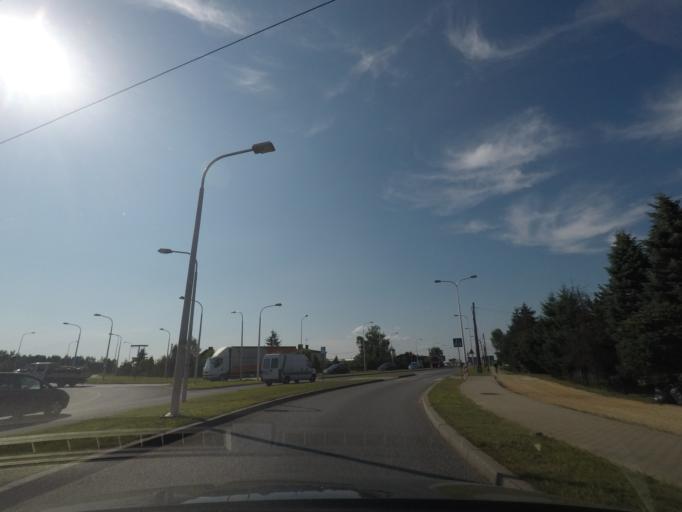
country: PL
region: Silesian Voivodeship
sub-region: Zory
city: Zory
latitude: 50.0616
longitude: 18.6635
